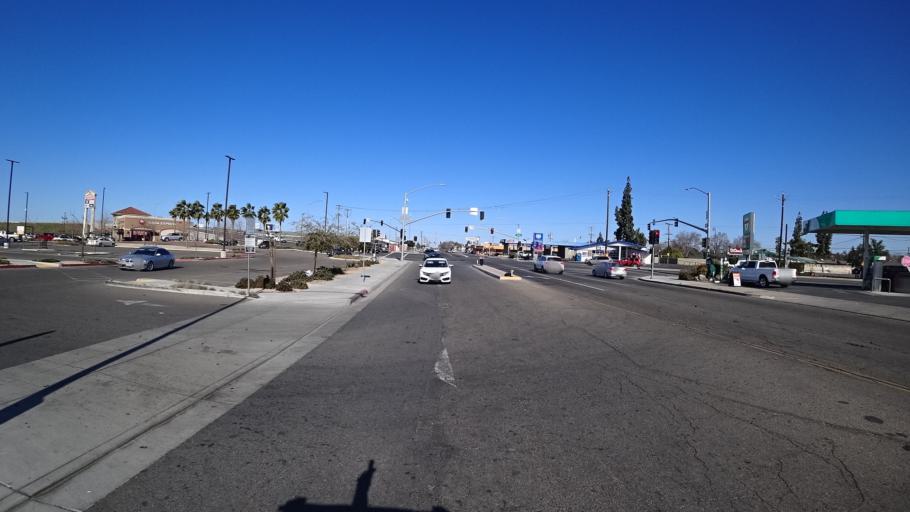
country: US
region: California
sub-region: Fresno County
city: West Park
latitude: 36.7715
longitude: -119.8338
